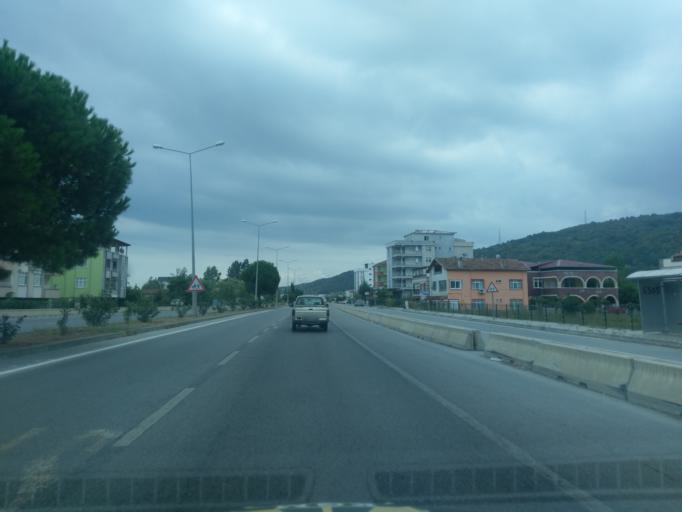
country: TR
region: Samsun
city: Taflan
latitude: 41.3950
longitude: 36.1985
